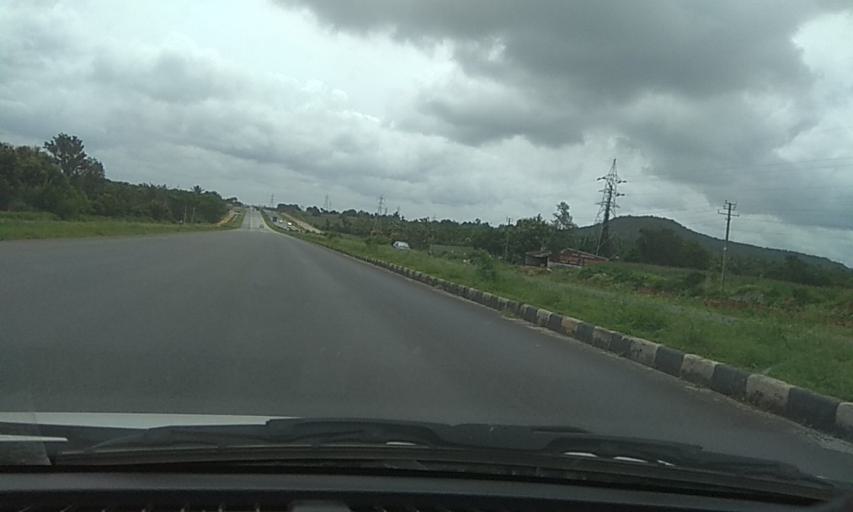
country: IN
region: Karnataka
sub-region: Davanagere
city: Mayakonda
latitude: 14.3722
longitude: 76.1203
